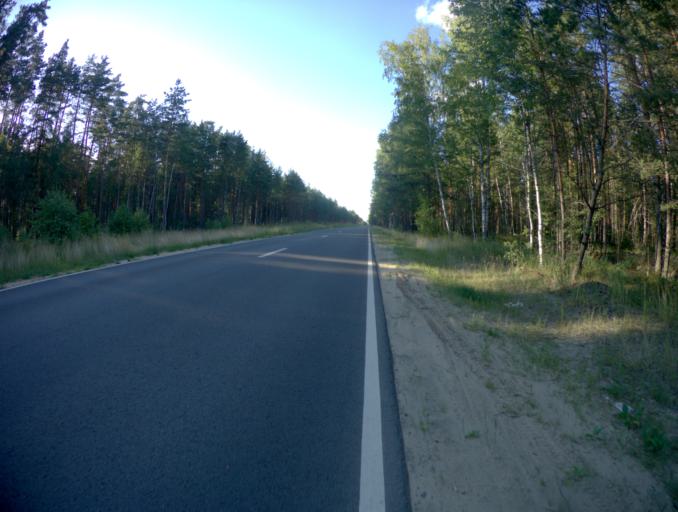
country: RU
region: Vladimir
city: Galitsy
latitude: 56.0307
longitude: 42.8613
